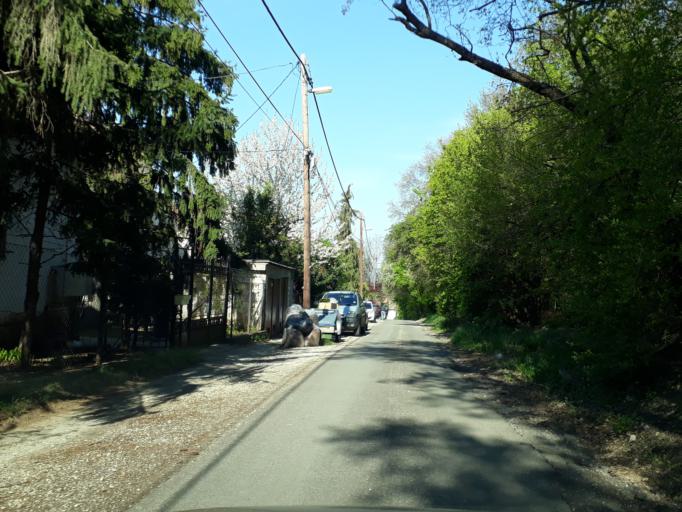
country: HU
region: Pest
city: Budakeszi
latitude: 47.5065
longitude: 18.9360
